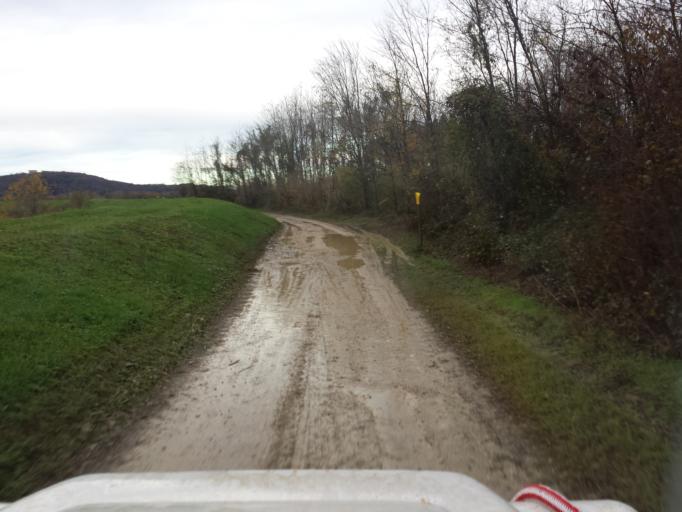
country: IT
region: Friuli Venezia Giulia
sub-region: Provincia di Gorizia
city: Mariano del Friuli
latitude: 45.9254
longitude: 13.4687
